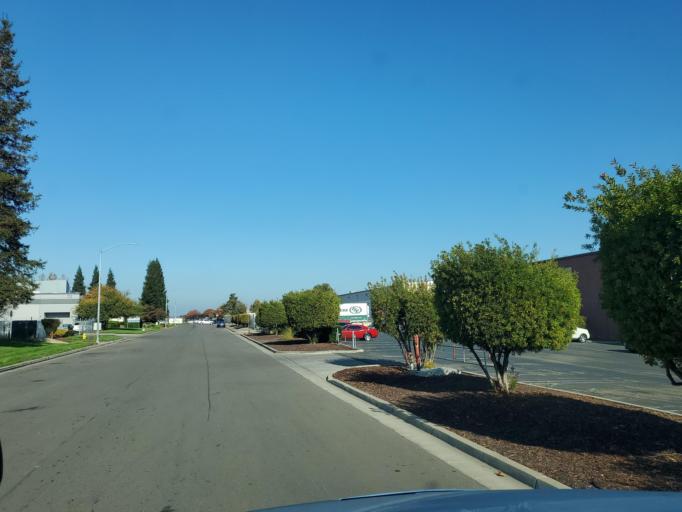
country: US
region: California
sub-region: San Joaquin County
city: Kennedy
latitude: 37.9091
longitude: -121.2332
